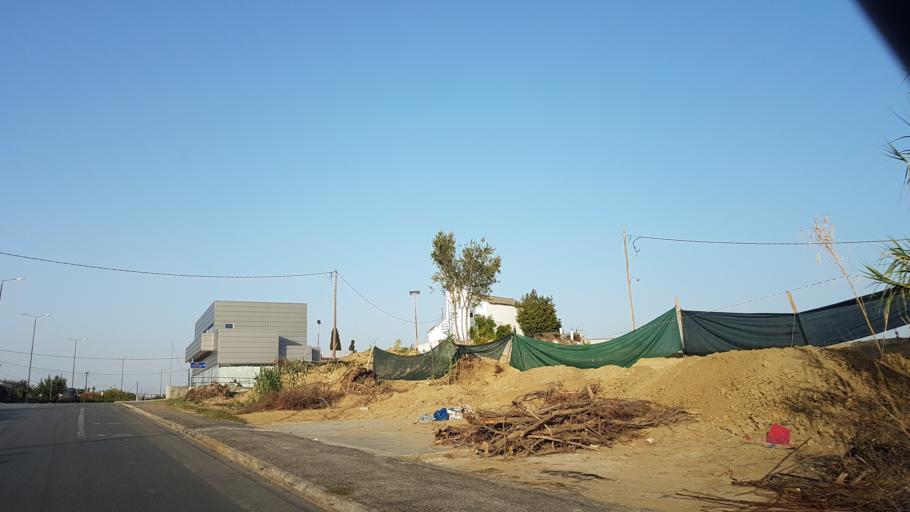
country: GR
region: Ionian Islands
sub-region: Nomos Kerkyras
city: Alepou
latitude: 39.6122
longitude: 19.9057
